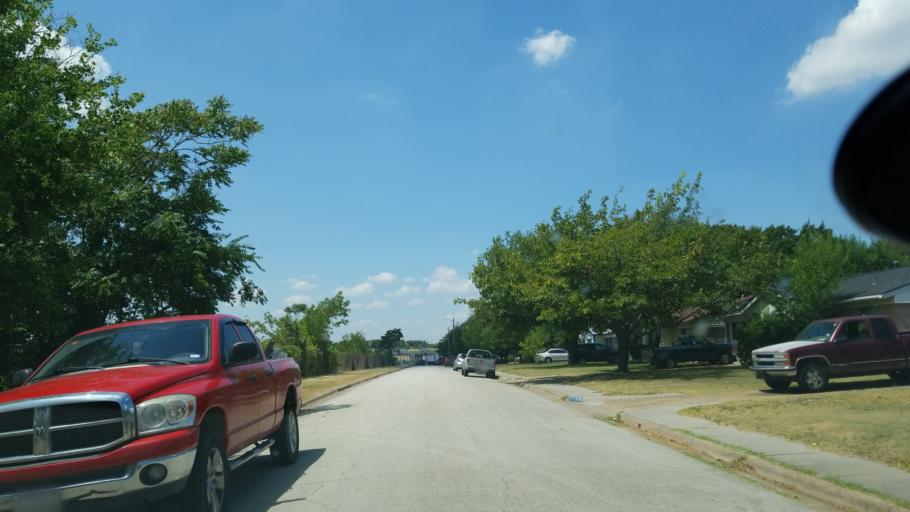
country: US
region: Texas
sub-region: Dallas County
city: Duncanville
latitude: 32.6654
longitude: -96.9028
